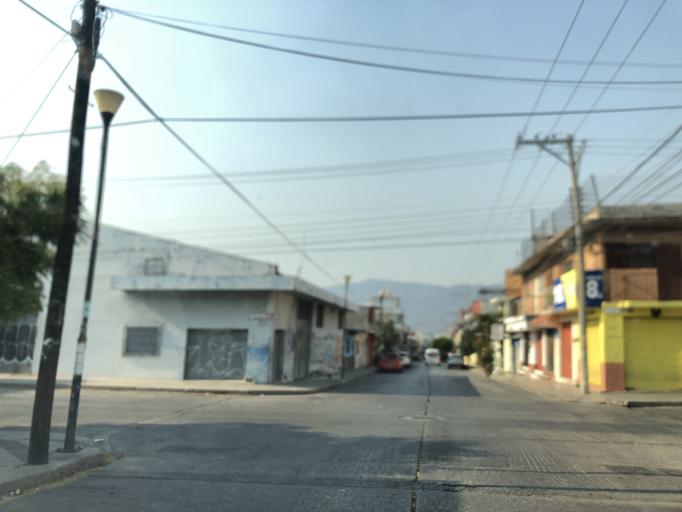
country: MX
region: Chiapas
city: Tuxtla Gutierrez
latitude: 16.7476
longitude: -93.1225
